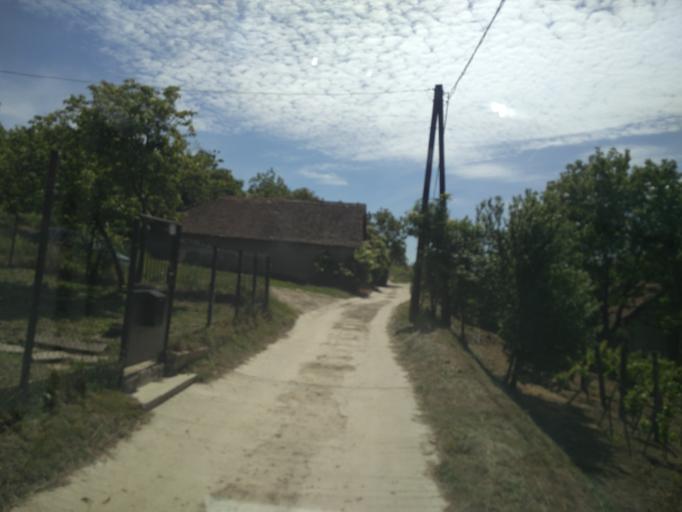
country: HU
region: Tolna
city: Szekszard
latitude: 46.3125
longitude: 18.6851
